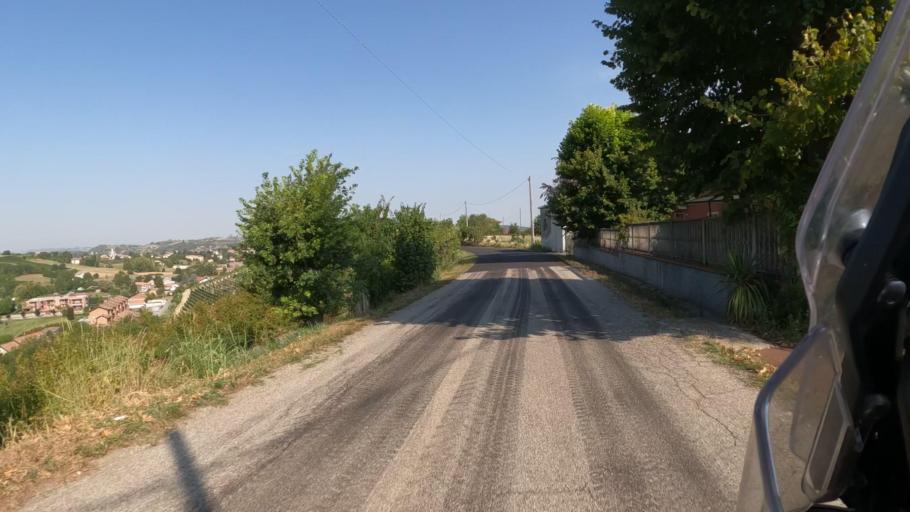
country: IT
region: Piedmont
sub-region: Provincia di Asti
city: Nizza Monferrato
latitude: 44.7643
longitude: 8.3759
